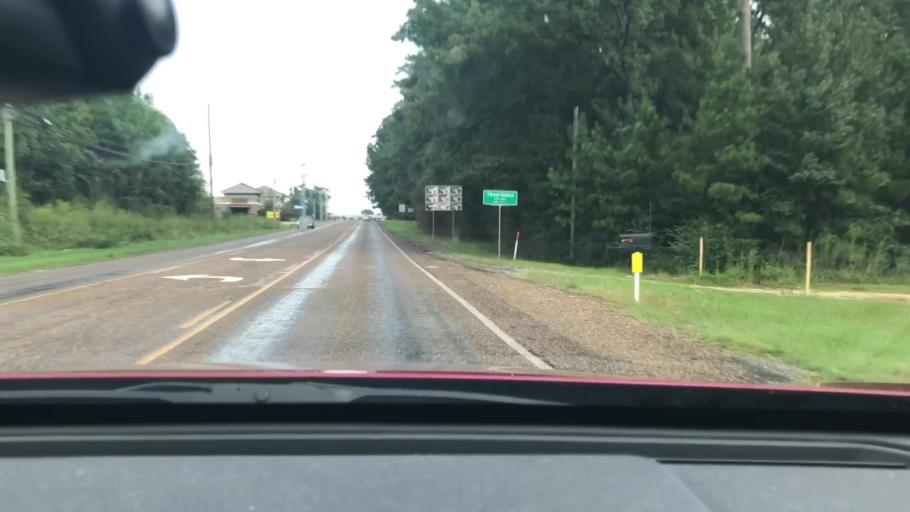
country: US
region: Texas
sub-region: Bowie County
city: Wake Village
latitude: 33.4435
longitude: -94.1048
